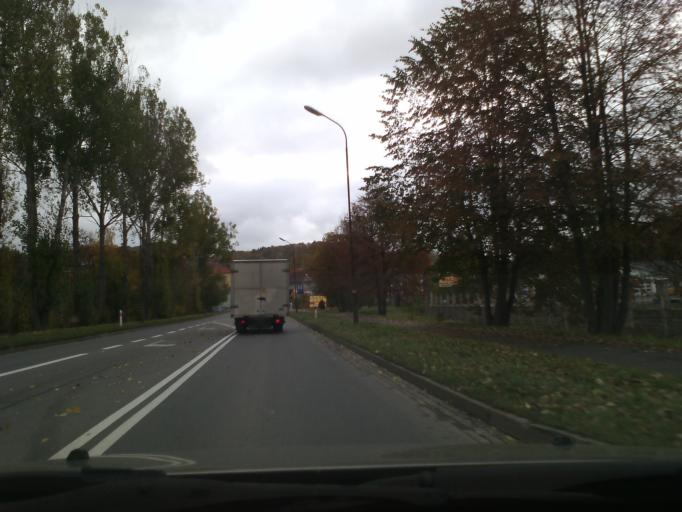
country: PL
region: Lower Silesian Voivodeship
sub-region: Powiat kamiennogorski
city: Kamienna Gora
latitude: 50.7879
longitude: 16.0379
